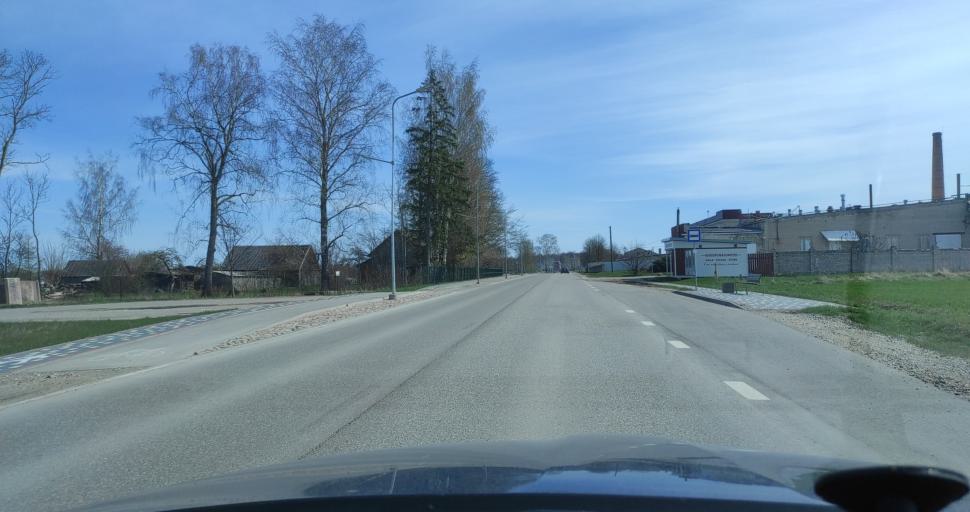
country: LV
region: Talsu Rajons
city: Talsi
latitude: 57.2323
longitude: 22.5540
